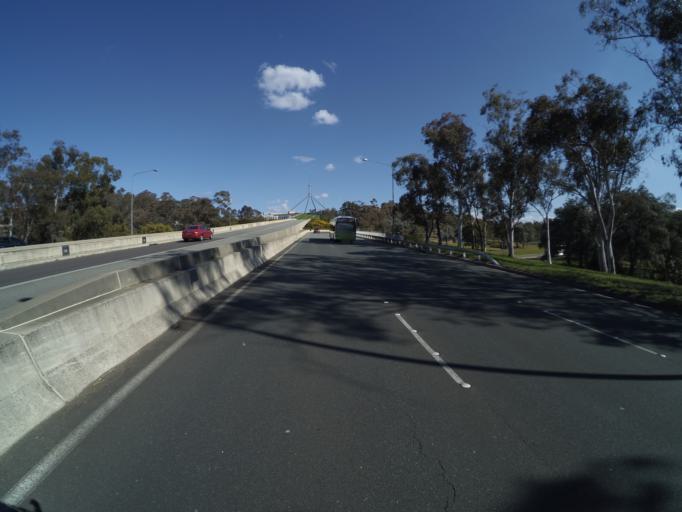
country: AU
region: Australian Capital Territory
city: Forrest
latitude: -35.3034
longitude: 149.1251
